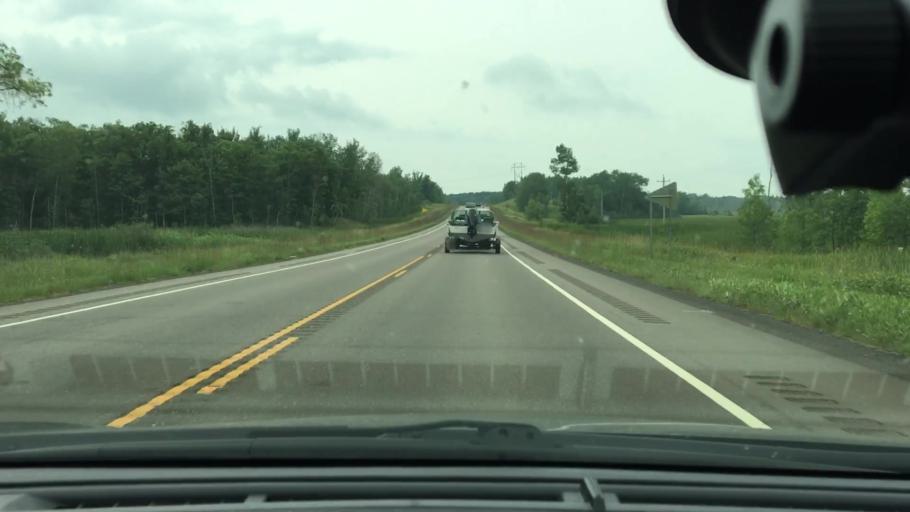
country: US
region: Minnesota
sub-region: Crow Wing County
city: Crosby
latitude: 46.6072
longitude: -93.9499
